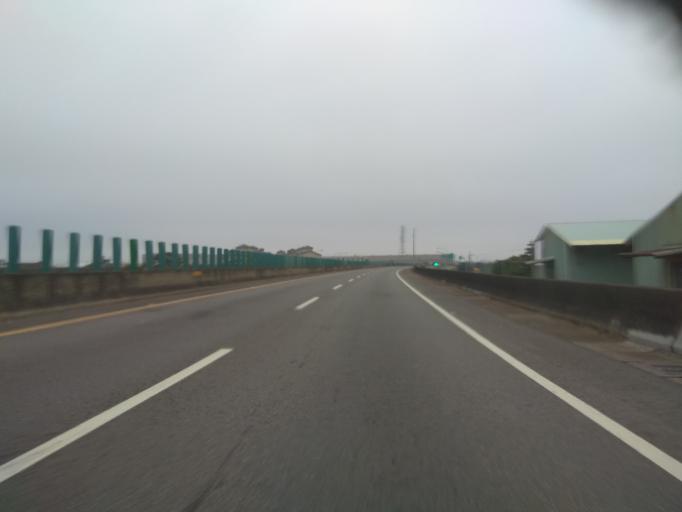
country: TW
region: Taiwan
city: Taoyuan City
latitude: 24.9811
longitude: 121.1318
